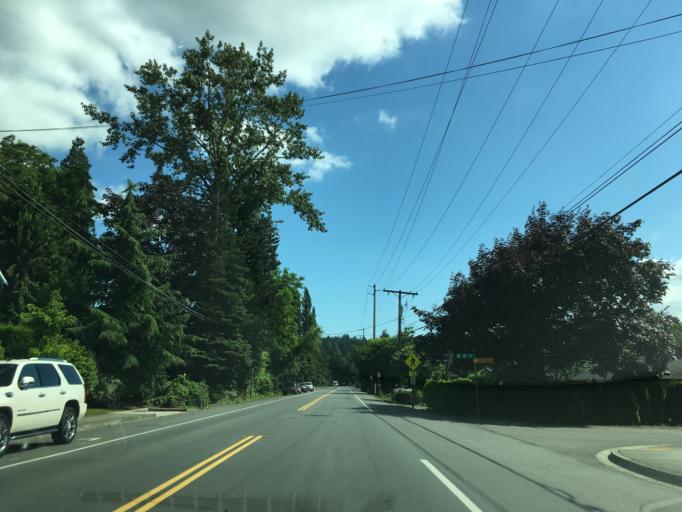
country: US
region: Washington
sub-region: King County
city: Kenmore
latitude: 47.7599
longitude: -122.2336
